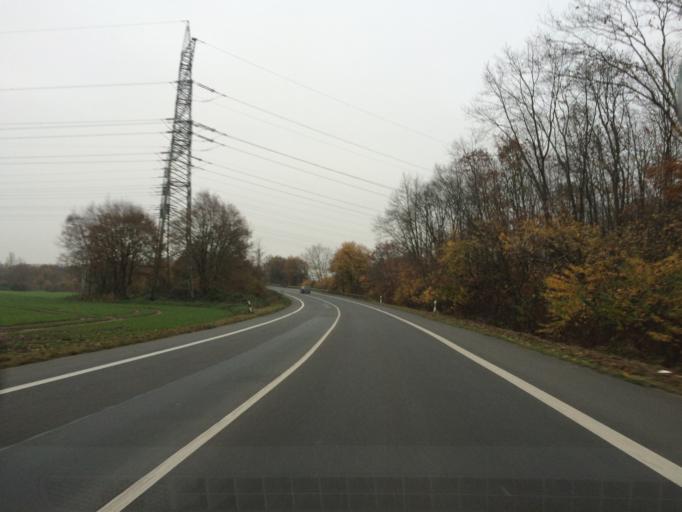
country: DE
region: North Rhine-Westphalia
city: Marl
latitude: 51.6965
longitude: 7.0696
